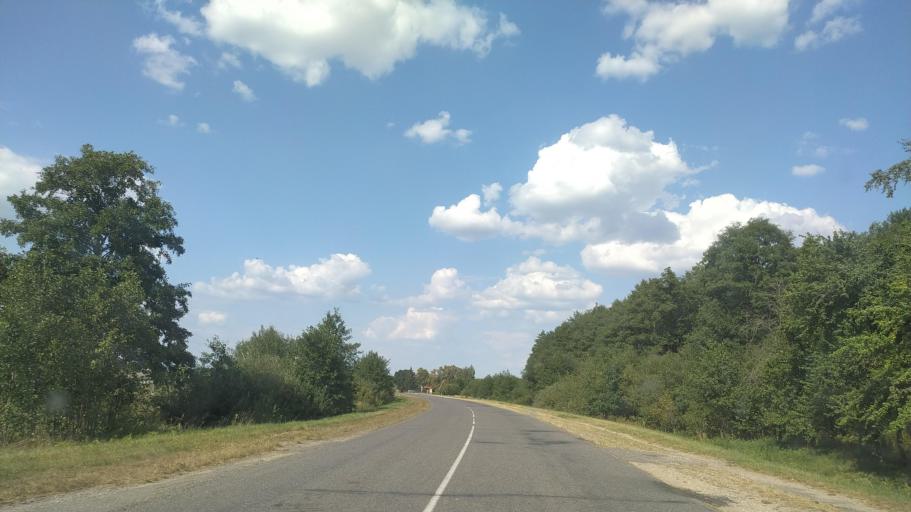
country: BY
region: Brest
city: Drahichyn
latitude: 52.1353
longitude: 25.1235
